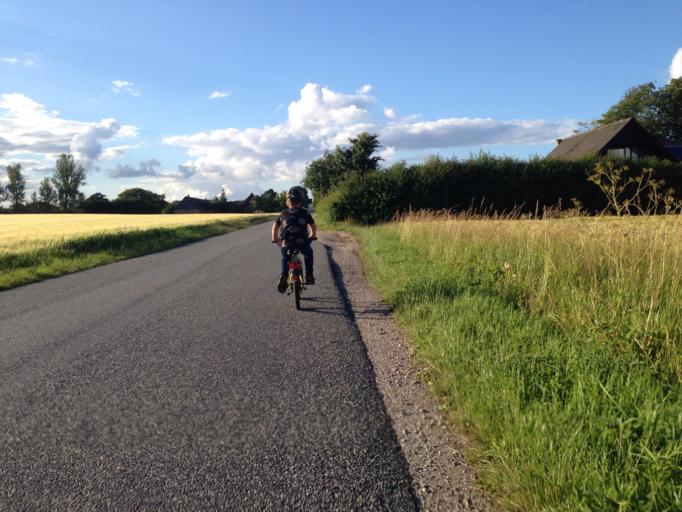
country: DK
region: South Denmark
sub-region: Middelfart Kommune
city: Norre Aby
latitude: 55.4768
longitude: 9.9035
